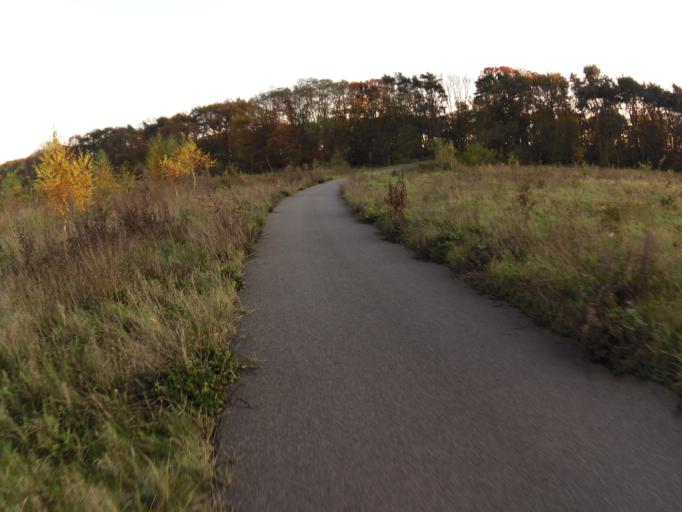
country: NL
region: North Brabant
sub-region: Gemeente Haaren
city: Haaren
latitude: 51.6705
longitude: 5.1909
